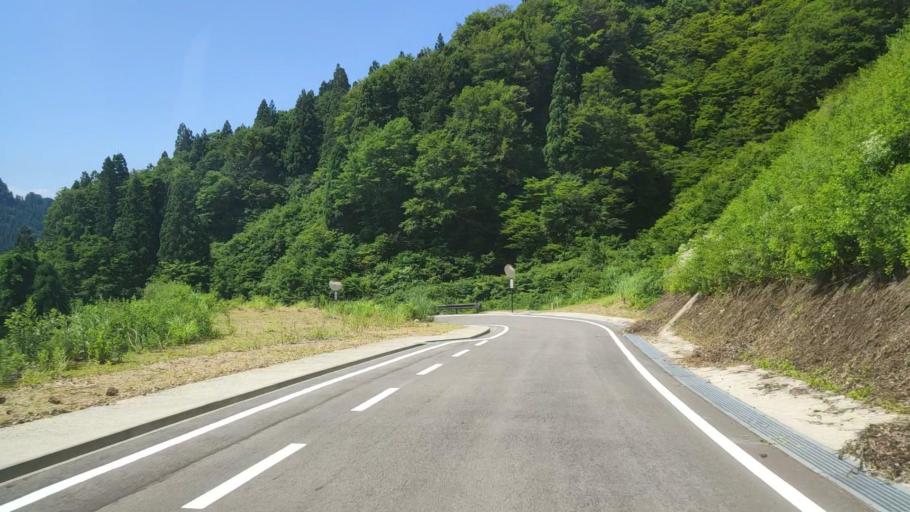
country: JP
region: Fukui
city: Katsuyama
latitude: 36.1442
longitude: 136.5201
